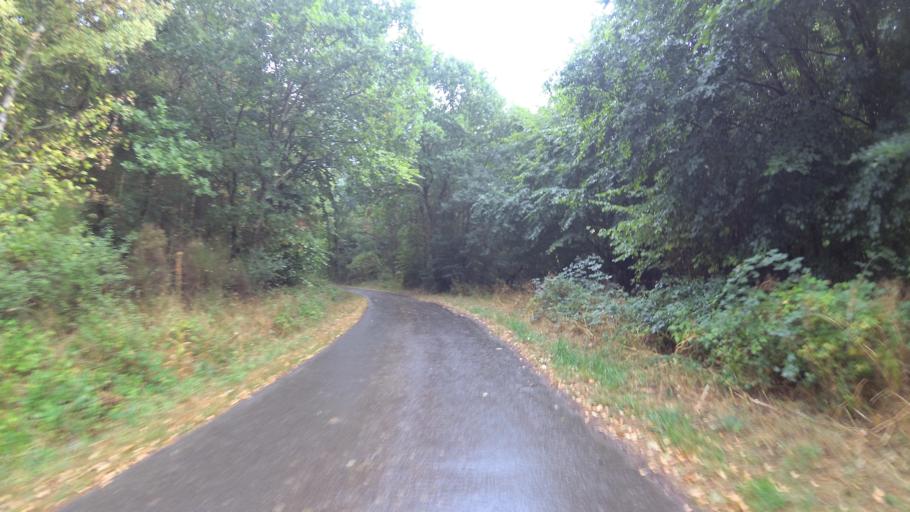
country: DE
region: Rheinland-Pfalz
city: Rorodt
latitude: 49.7625
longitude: 7.0854
